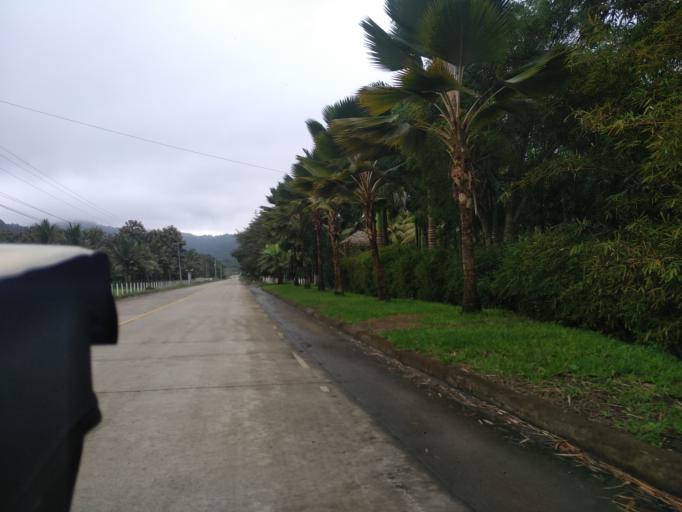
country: EC
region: Manabi
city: Jipijapa
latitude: -1.6658
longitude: -80.8123
